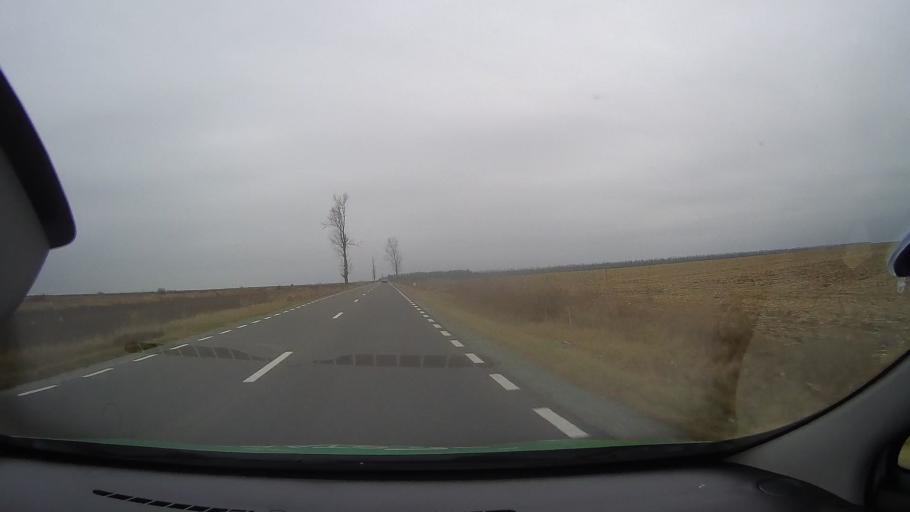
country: RO
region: Ialomita
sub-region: Comuna Scanteia
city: Iazu
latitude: 44.7118
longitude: 27.4192
